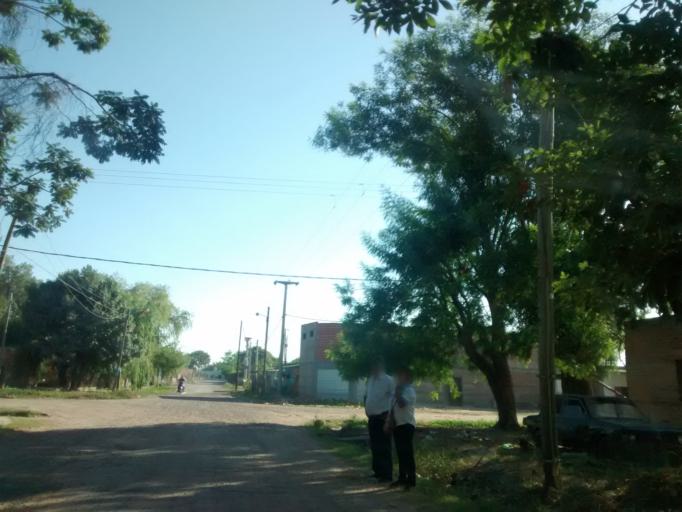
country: AR
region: Chaco
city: Resistencia
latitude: -27.4610
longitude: -58.9615
